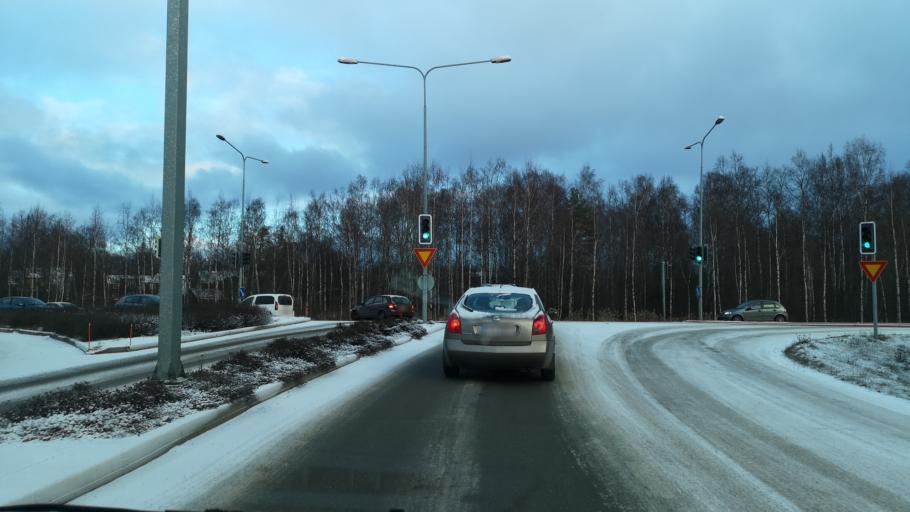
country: FI
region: Ostrobothnia
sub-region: Vaasa
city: Vaasa
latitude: 63.1108
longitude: 21.6190
